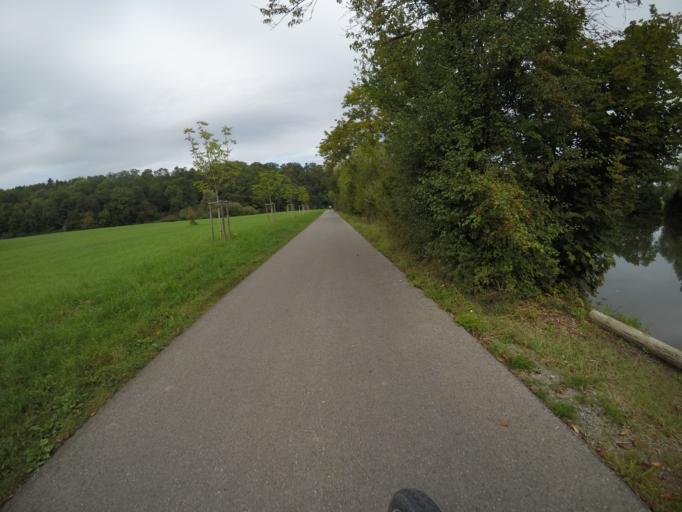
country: DE
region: Baden-Wuerttemberg
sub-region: Regierungsbezirk Stuttgart
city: Marbach am Neckar
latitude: 48.8952
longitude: 9.2606
